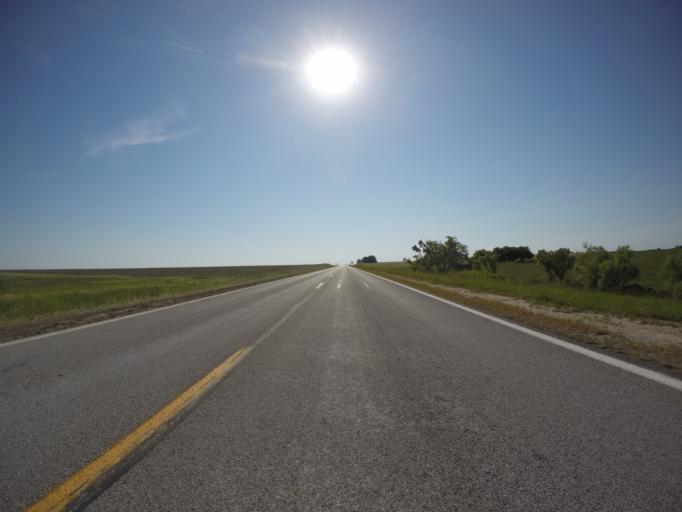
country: US
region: Nebraska
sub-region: Pawnee County
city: Pawnee City
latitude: 40.0446
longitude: -96.3572
